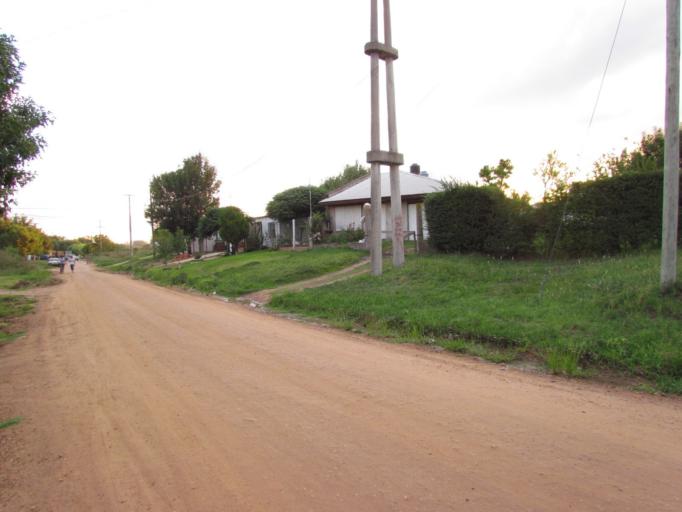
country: AR
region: Entre Rios
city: Concepcion del Uruguay
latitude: -32.4956
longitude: -58.2561
